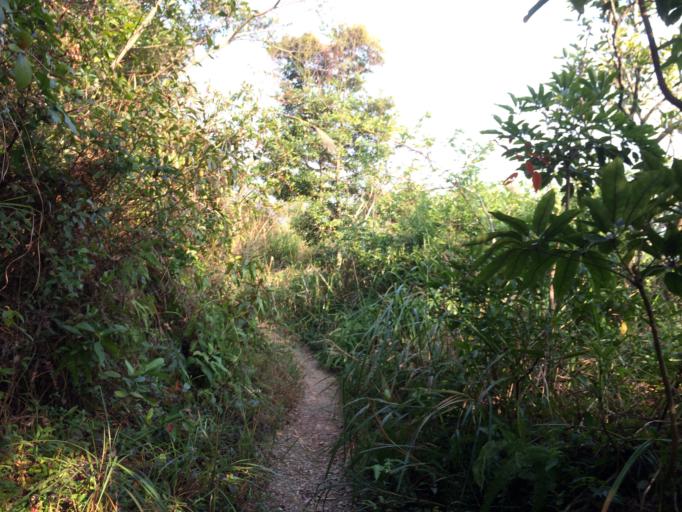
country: HK
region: Tai Po
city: Tai Po
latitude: 22.4509
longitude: 114.2293
